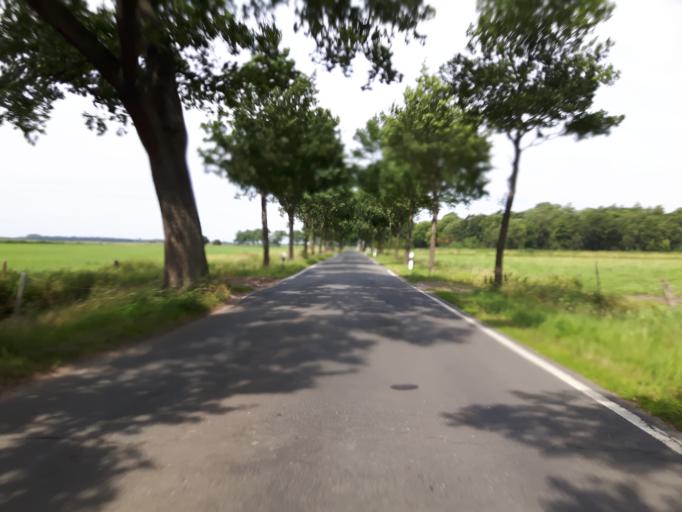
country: DE
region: Lower Saxony
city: Rastede
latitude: 53.3291
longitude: 8.2637
